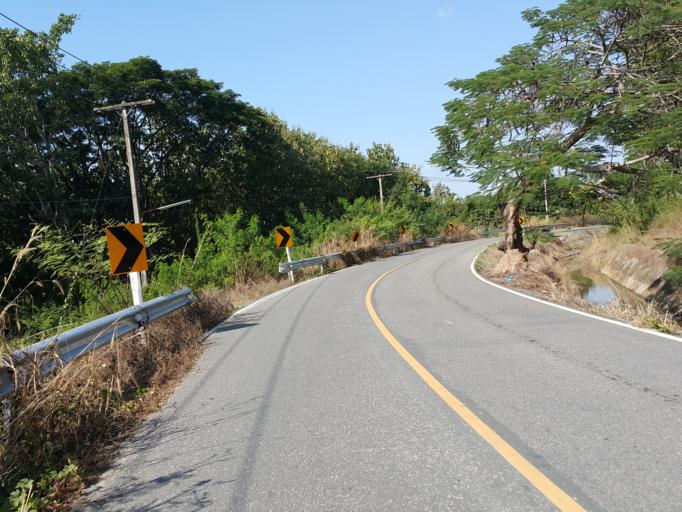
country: TH
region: Chiang Mai
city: San Kamphaeng
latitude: 18.7700
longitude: 99.1727
